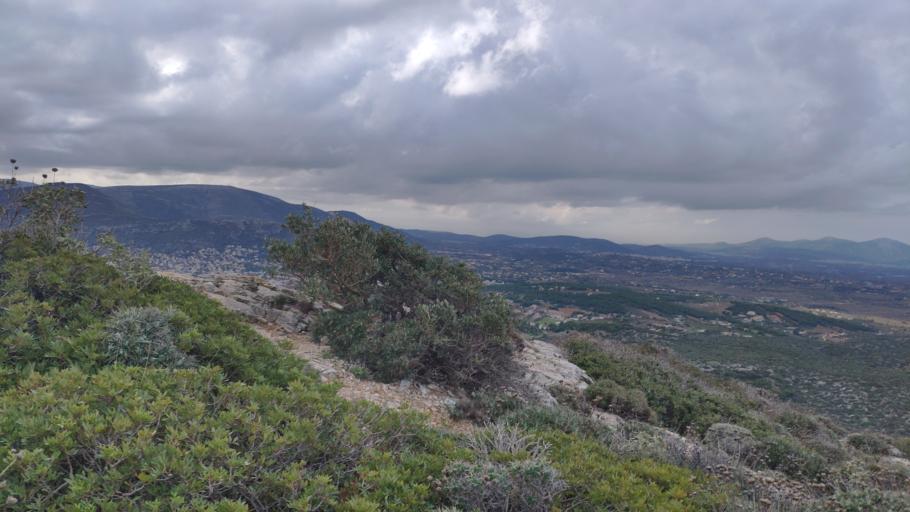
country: GR
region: Attica
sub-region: Nomarchia Anatolikis Attikis
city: Limin Mesoyaias
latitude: 37.9110
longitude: 24.0222
